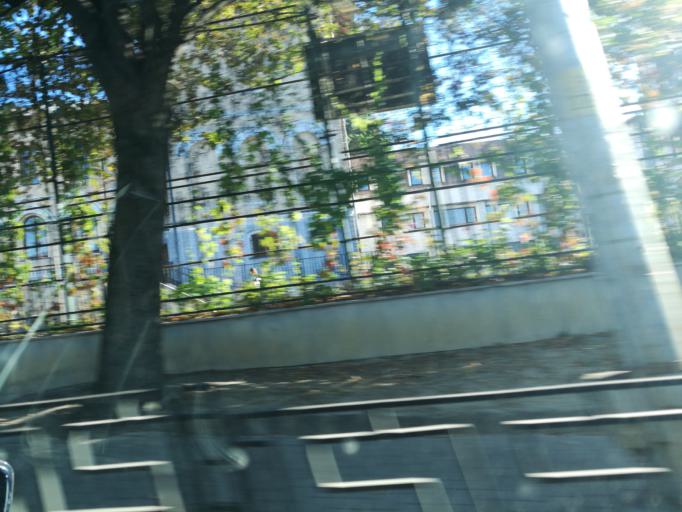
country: RO
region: Iasi
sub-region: Municipiul Iasi
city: Iasi
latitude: 47.1668
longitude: 27.5775
